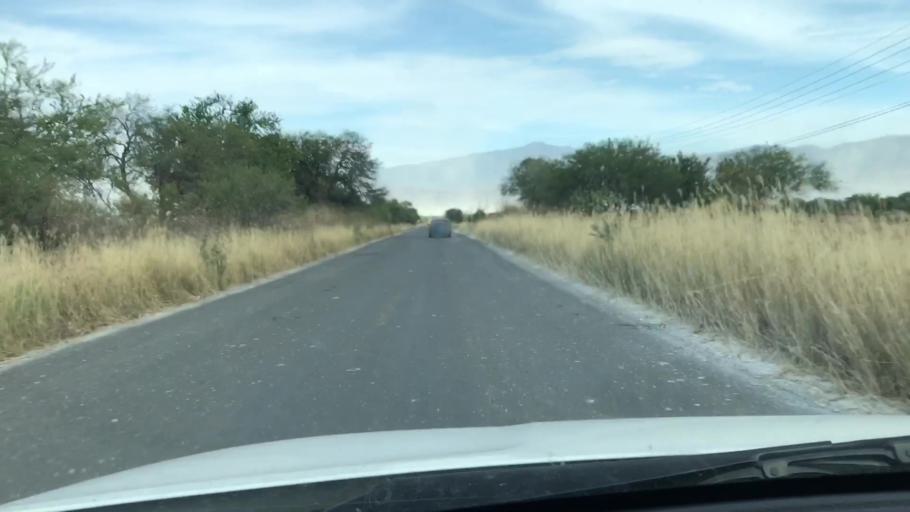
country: MX
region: Jalisco
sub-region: Zacoalco de Torres
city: Barranca de Otates (Barranca de Otatan)
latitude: 20.2850
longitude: -103.6144
